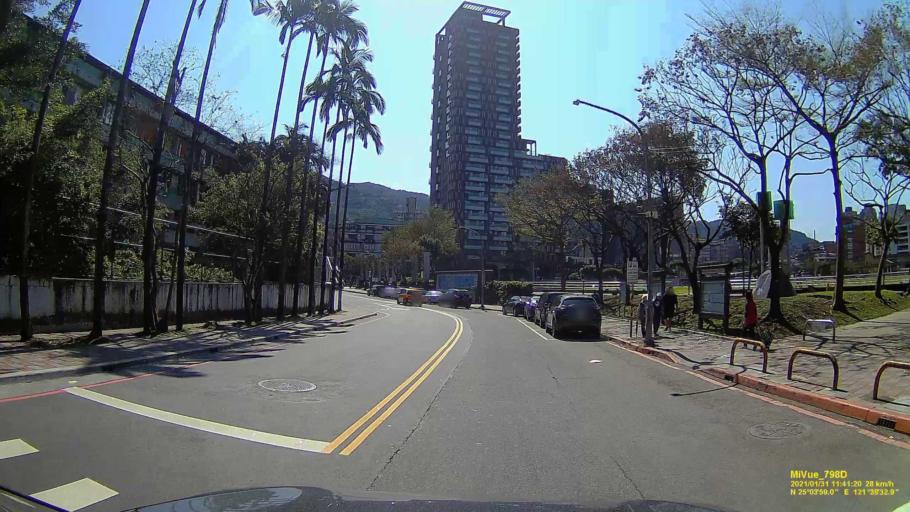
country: TW
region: Taiwan
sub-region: Keelung
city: Keelung
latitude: 25.0662
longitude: 121.6592
